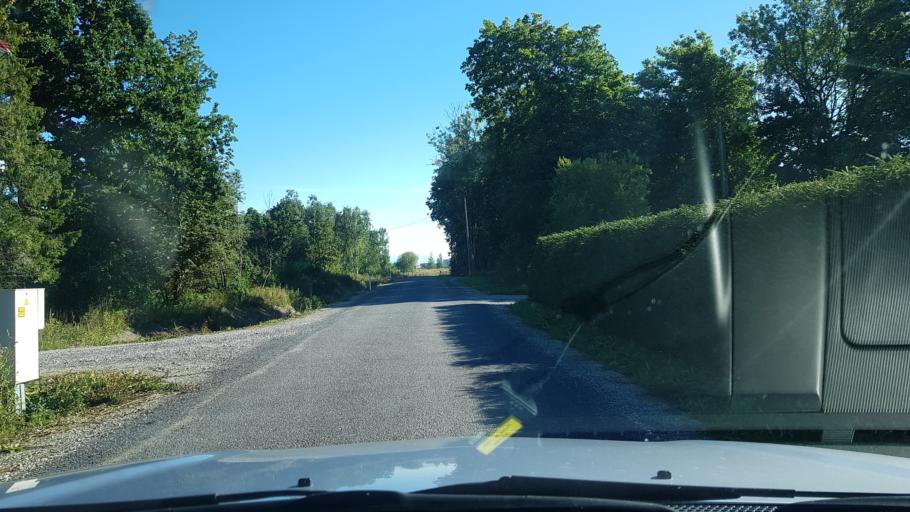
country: EE
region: Harju
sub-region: Joelaehtme vald
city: Loo
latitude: 59.4213
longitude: 24.9179
